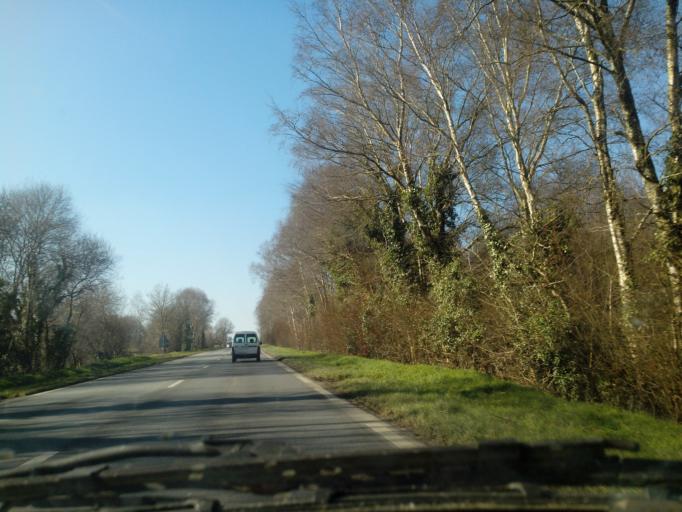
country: FR
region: Brittany
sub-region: Departement des Cotes-d'Armor
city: Plemet
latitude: 48.1700
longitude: -2.6067
